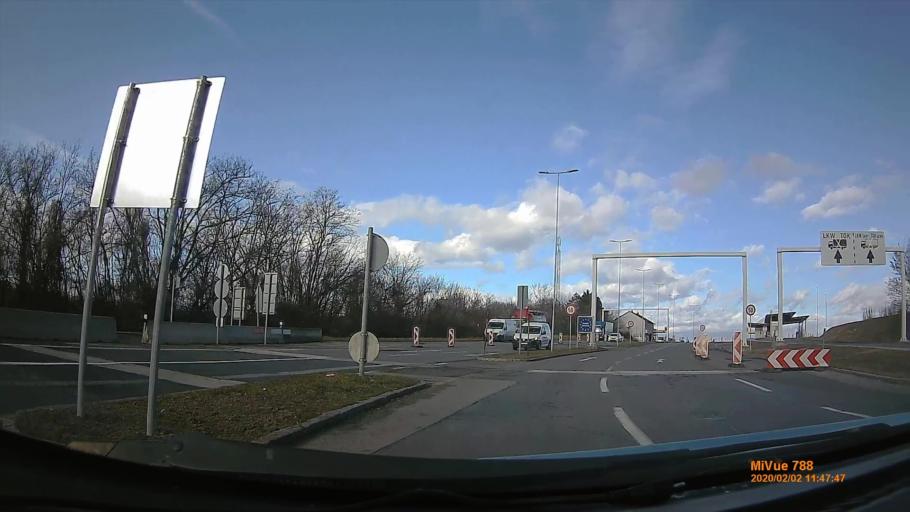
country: AT
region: Burgenland
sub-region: Eisenstadt-Umgebung
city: Klingenbach
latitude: 47.7412
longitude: 16.5454
